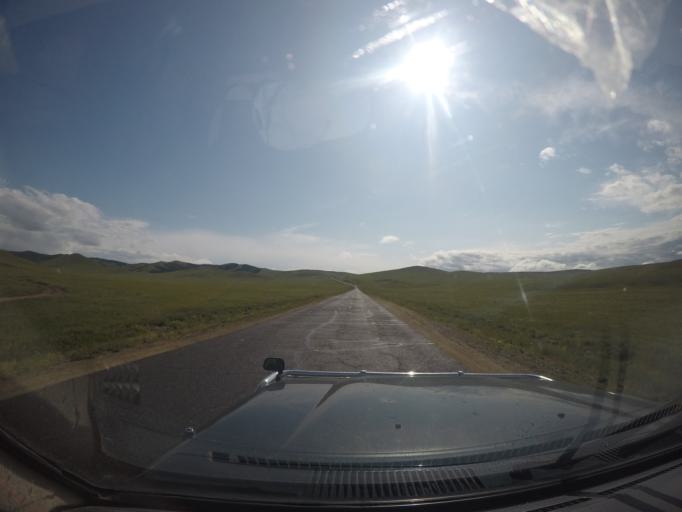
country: MN
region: Hentiy
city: Modot
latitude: 47.8061
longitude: 108.7839
